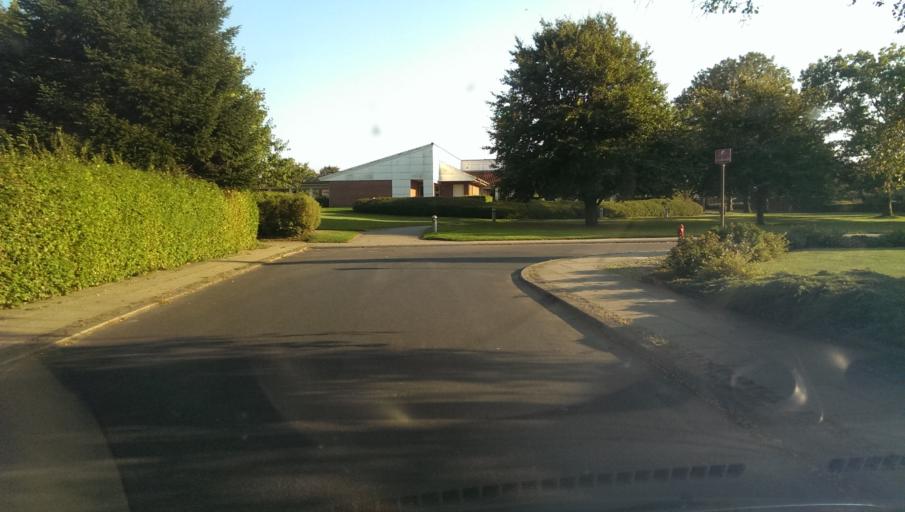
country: DK
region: South Denmark
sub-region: Esbjerg Kommune
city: Bramming
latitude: 55.4762
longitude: 8.7981
